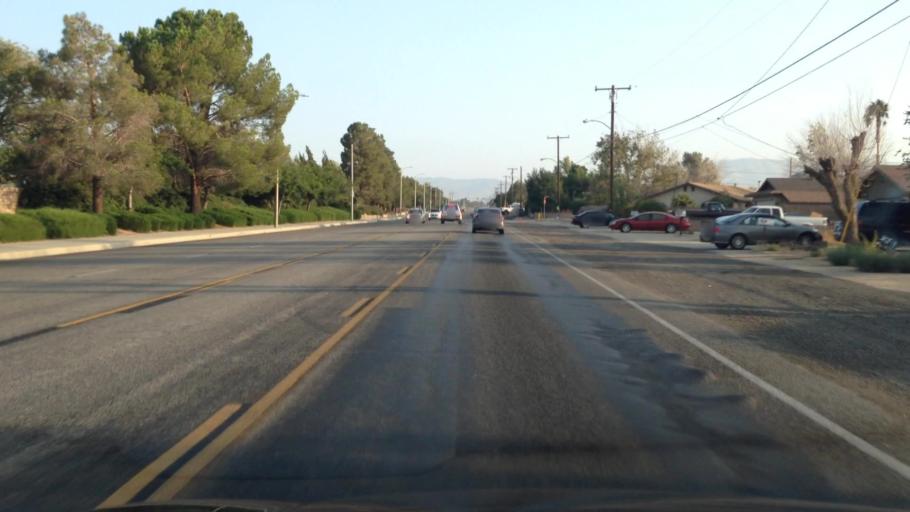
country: US
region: California
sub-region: Los Angeles County
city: Quartz Hill
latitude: 34.6579
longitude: -118.1834
